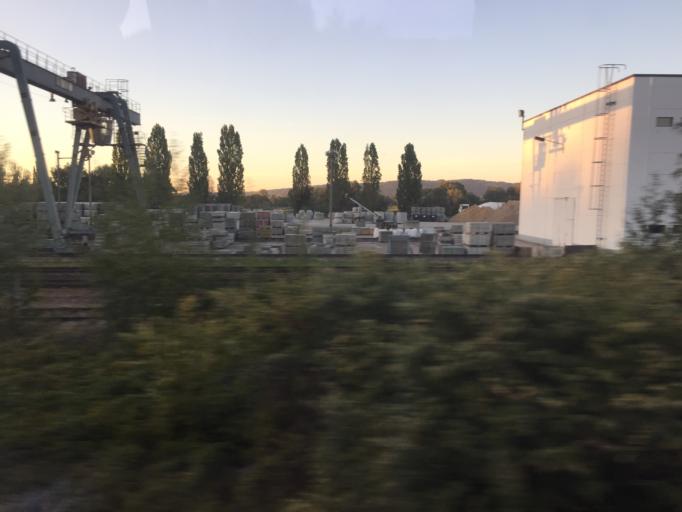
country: DE
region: Saxony
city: Pirna
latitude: 50.9595
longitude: 13.9086
